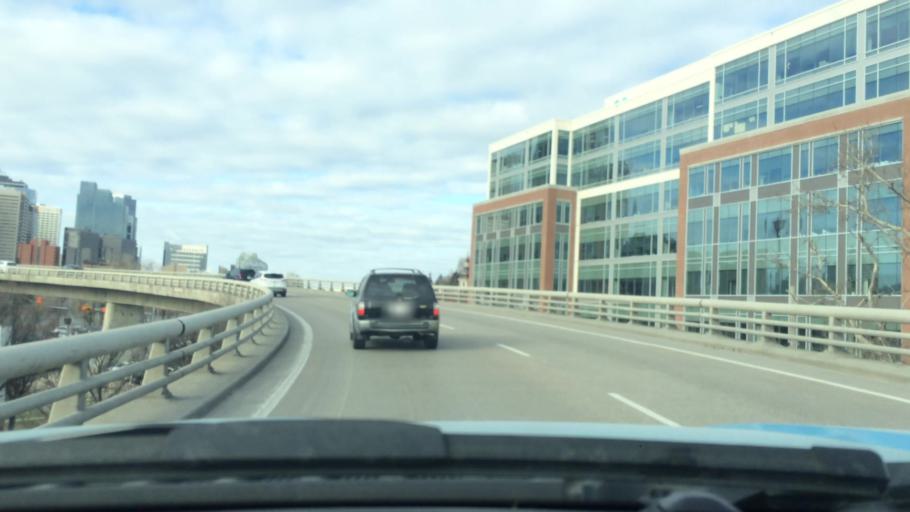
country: CA
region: Alberta
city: Calgary
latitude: 51.0507
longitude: -114.0492
